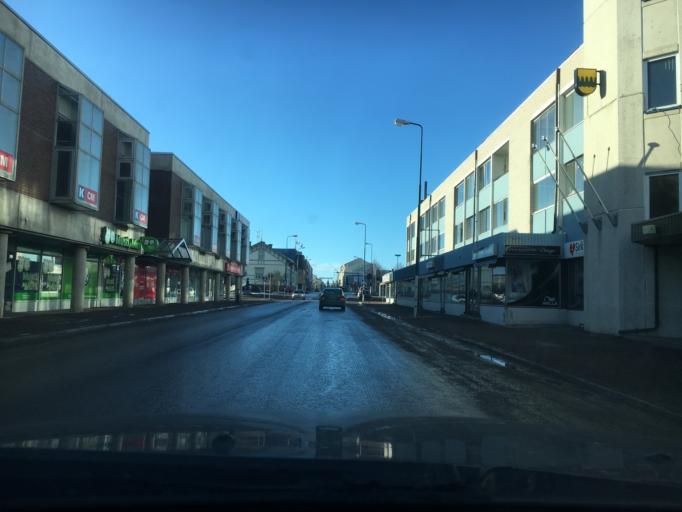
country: FI
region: Kainuu
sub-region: Kajaani
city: Kajaani
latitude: 64.2233
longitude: 27.7368
